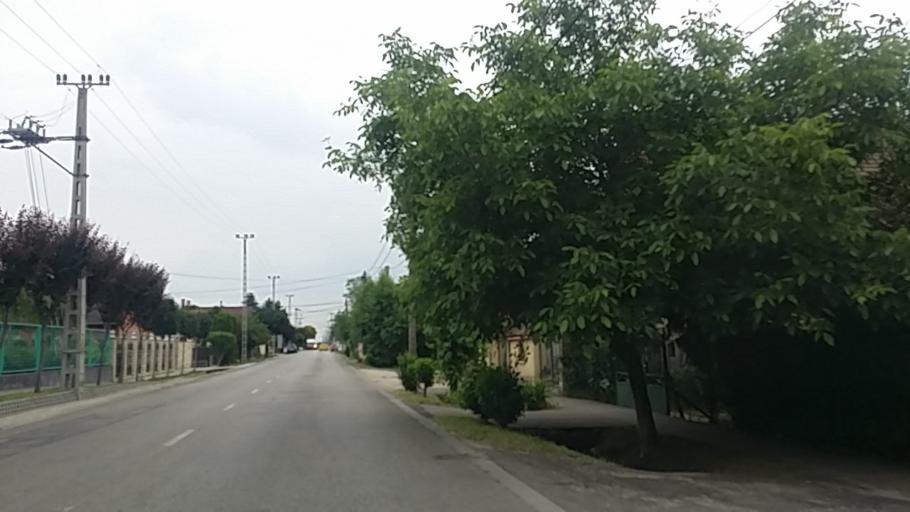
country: HU
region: Pest
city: Vecses
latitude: 47.4124
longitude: 19.2482
